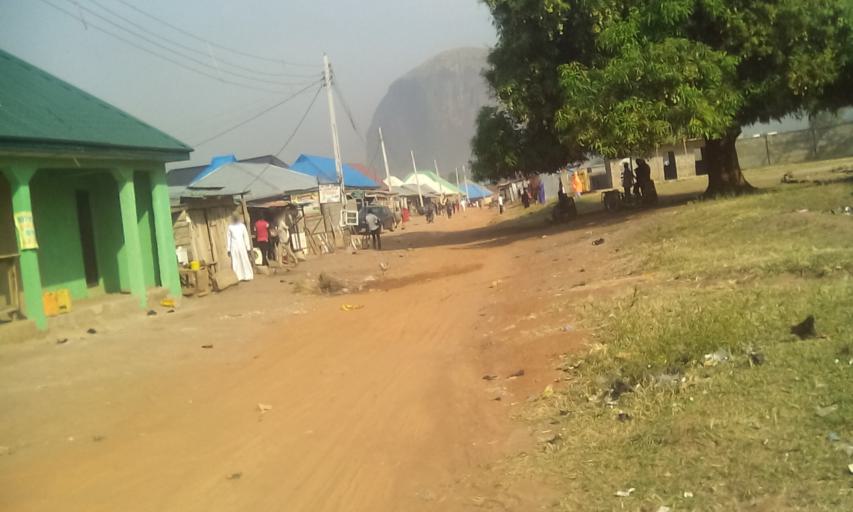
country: NG
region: Abuja Federal Capital Territory
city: Madala
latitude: 9.1079
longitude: 7.2419
